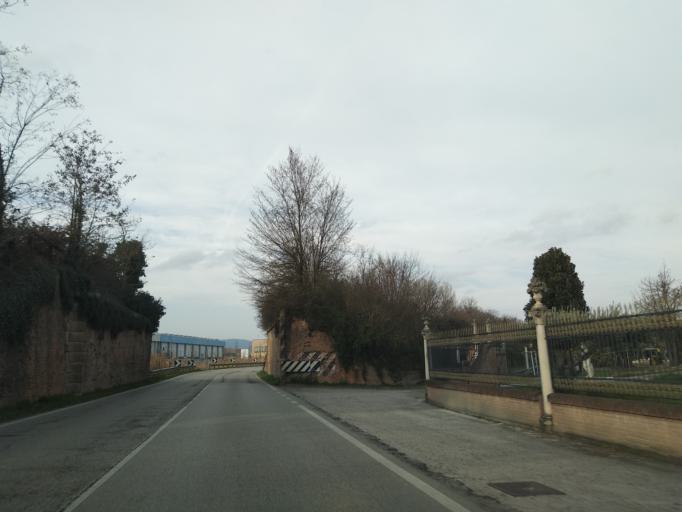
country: IT
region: Veneto
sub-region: Provincia di Vicenza
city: Ponte di Nanto
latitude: 45.4122
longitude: 11.5850
